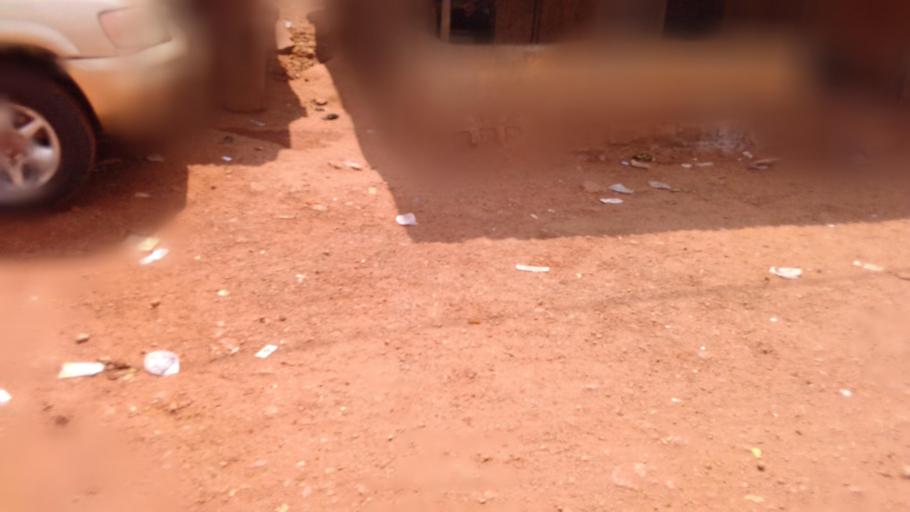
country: SL
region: Southern Province
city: Mogbwemo
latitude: 7.7910
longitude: -12.2970
